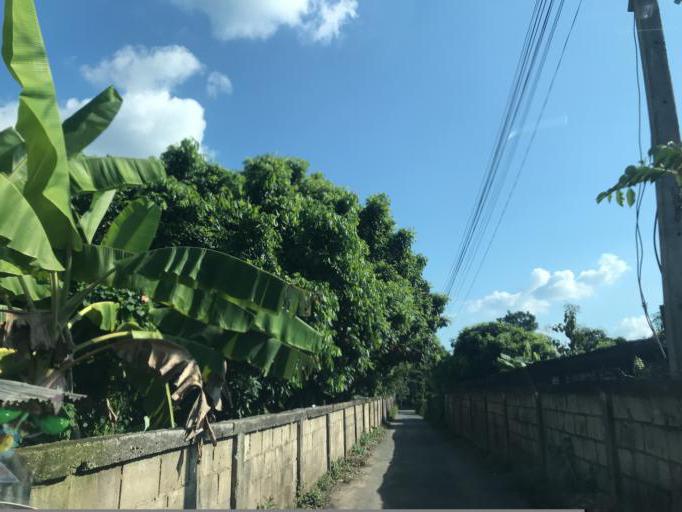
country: TH
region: Chiang Mai
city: San Pa Tong
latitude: 18.6547
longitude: 98.8633
